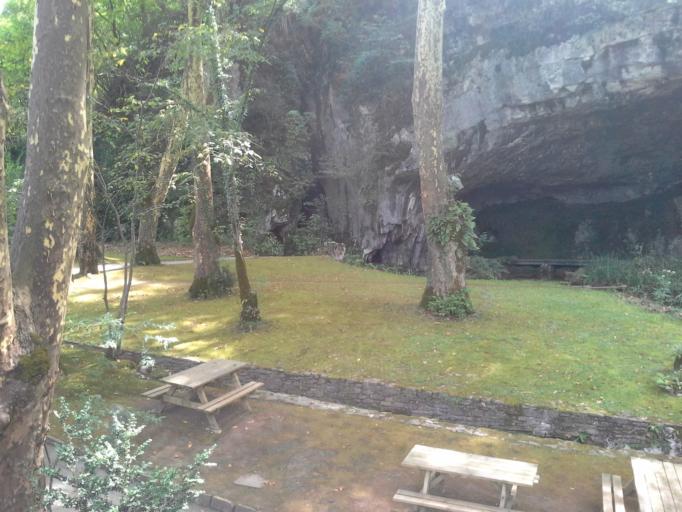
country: ES
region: Navarre
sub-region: Provincia de Navarra
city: Zugarramurdi
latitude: 43.2685
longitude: -1.5716
